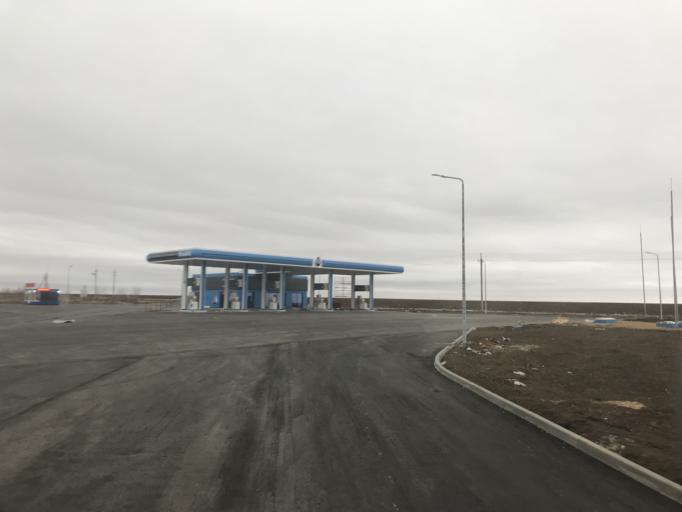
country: KZ
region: Batys Qazaqstan
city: Peremetnoe
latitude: 51.6475
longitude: 51.0119
